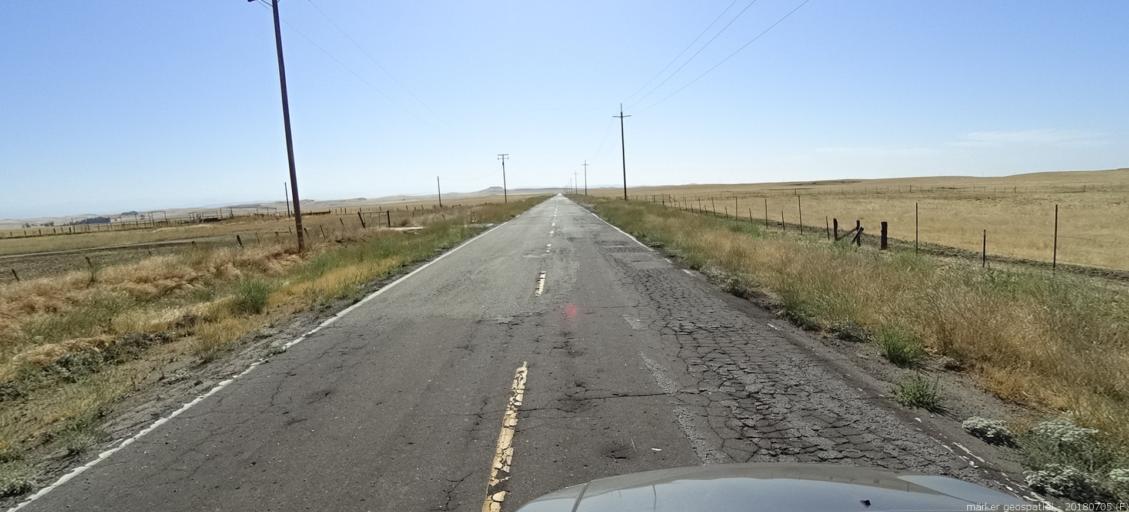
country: US
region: California
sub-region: Madera County
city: Madera Acres
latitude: 37.1267
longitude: -120.0396
